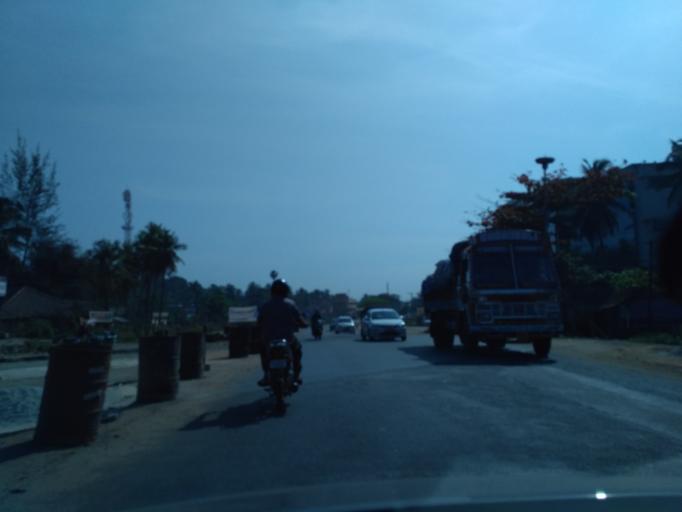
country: IN
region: Karnataka
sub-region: Dakshina Kannada
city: Mangalore
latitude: 12.8713
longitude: 74.8938
